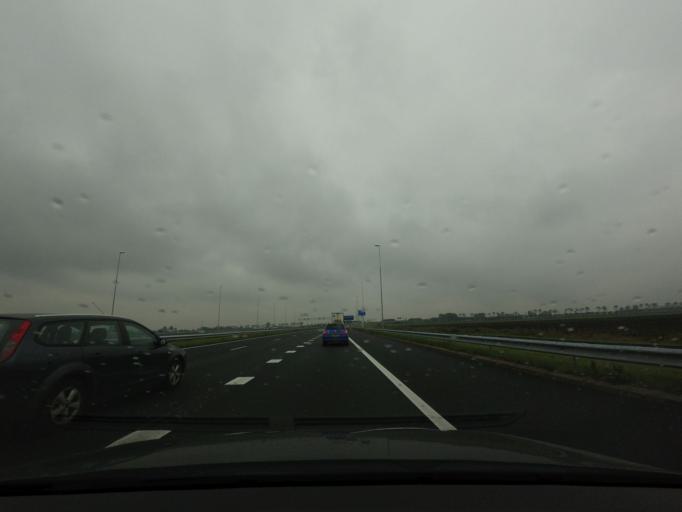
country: NL
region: North Holland
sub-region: Gemeente Haarlemmermeer
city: Hoofddorp
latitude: 52.3470
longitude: 4.7359
